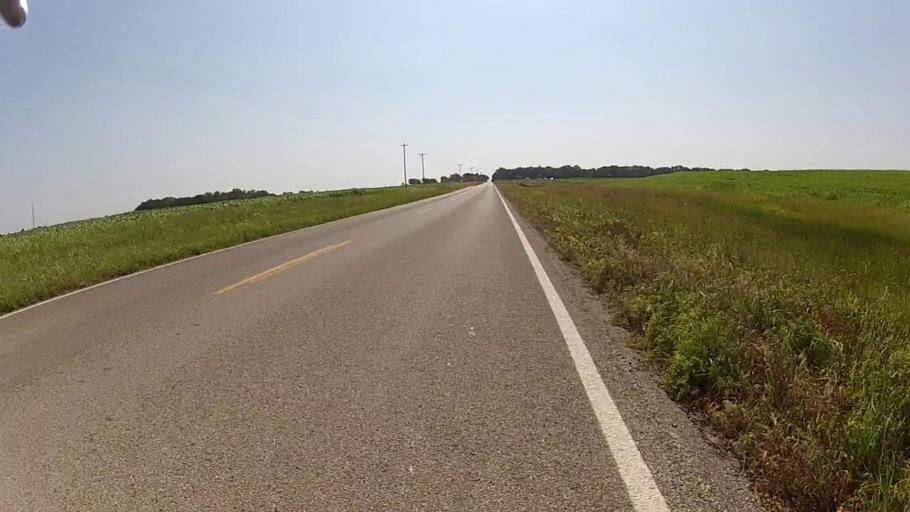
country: US
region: Kansas
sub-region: Montgomery County
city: Independence
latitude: 37.1930
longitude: -95.7484
